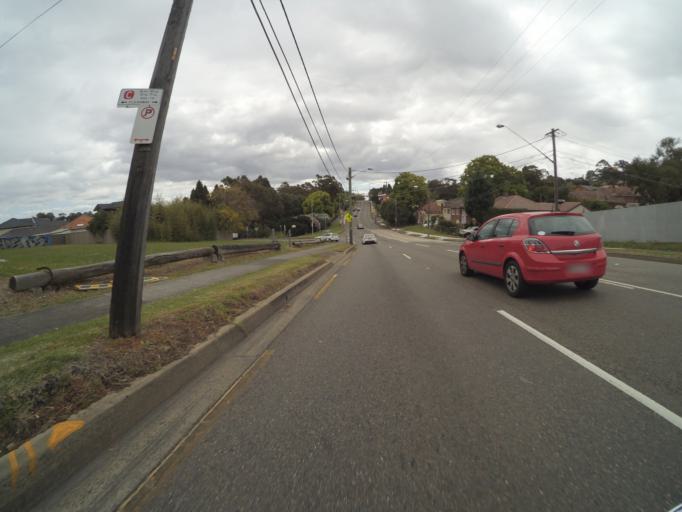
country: AU
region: New South Wales
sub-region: Kogarah
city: Hurstville Grove
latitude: -33.9742
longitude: 151.1019
